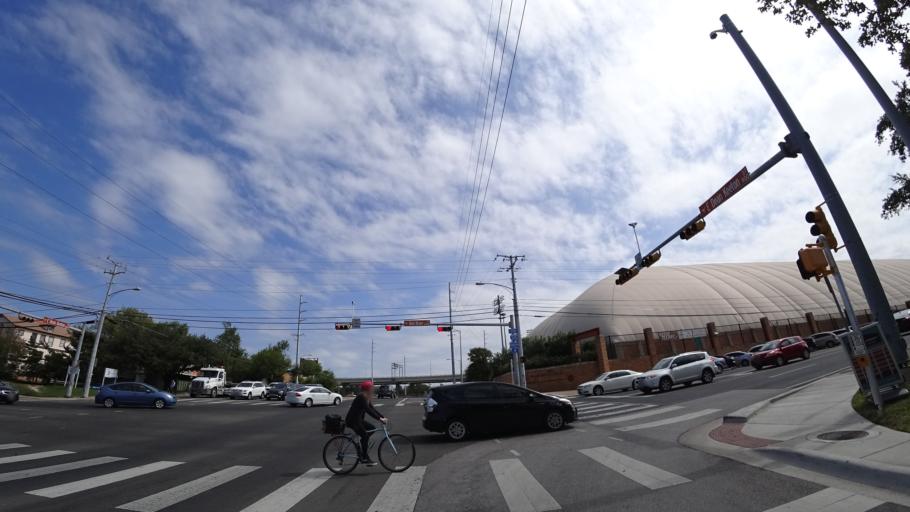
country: US
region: Texas
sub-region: Travis County
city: Austin
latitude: 30.2871
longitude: -97.7270
